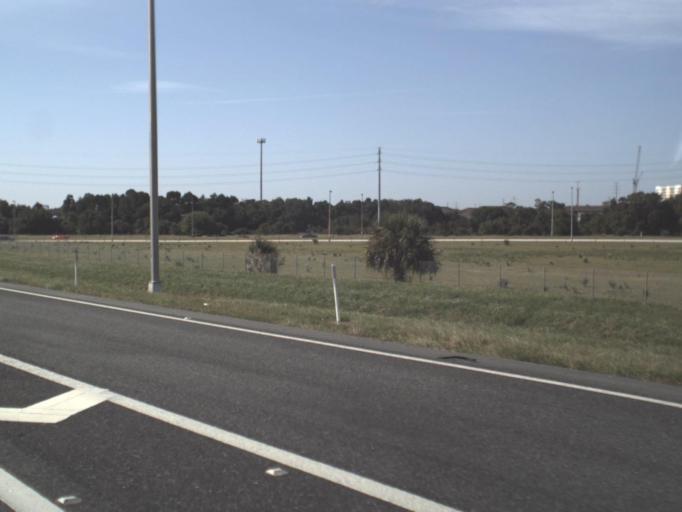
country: US
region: Florida
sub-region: Osceola County
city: Celebration
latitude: 28.3379
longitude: -81.5197
